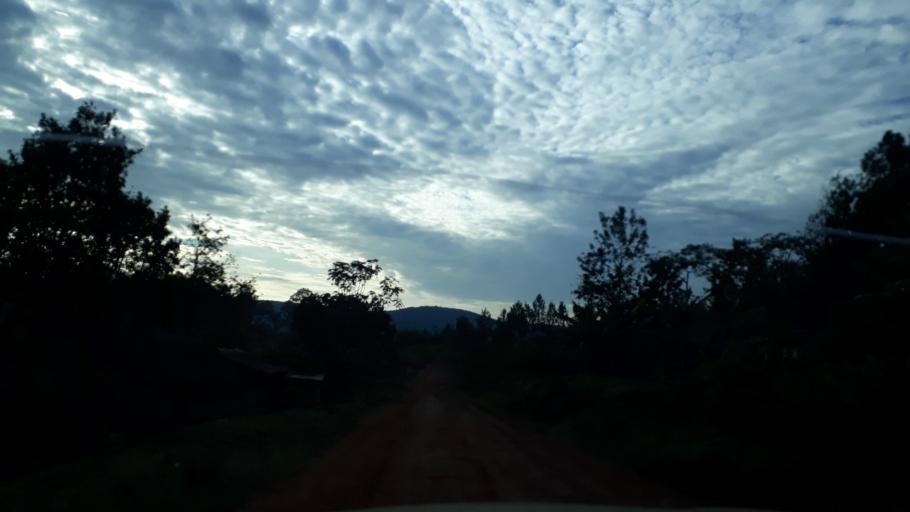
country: UG
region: Northern Region
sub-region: Zombo District
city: Paidha
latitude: 2.2312
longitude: 30.8179
